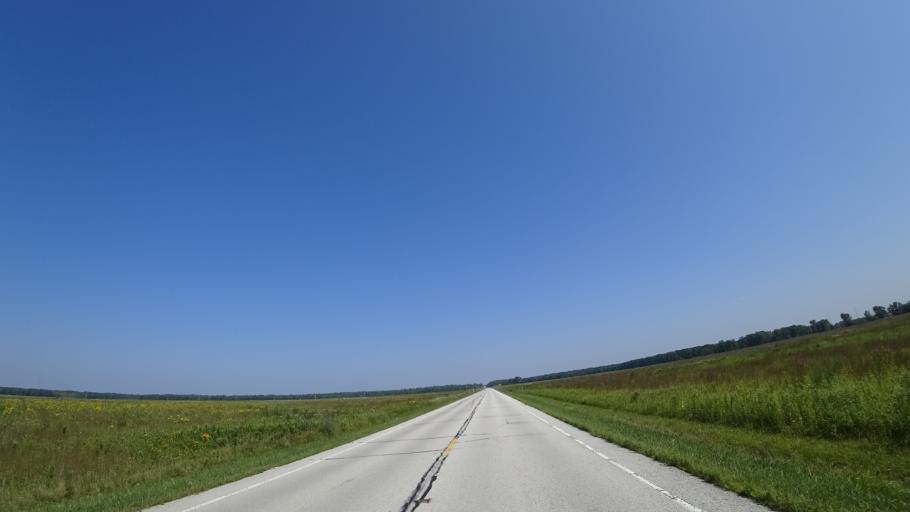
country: US
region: Illinois
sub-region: Cook County
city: Country Club Hills
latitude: 41.5387
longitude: -87.7518
